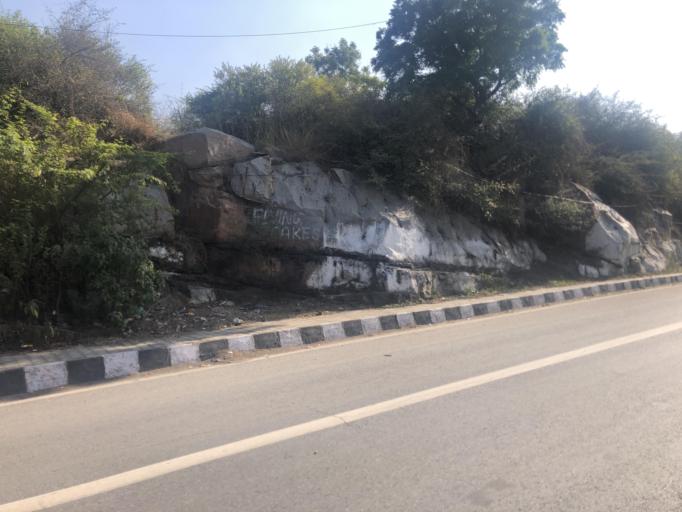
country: IN
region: NCT
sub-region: Central Delhi
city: Karol Bagh
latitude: 28.5504
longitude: 77.1642
